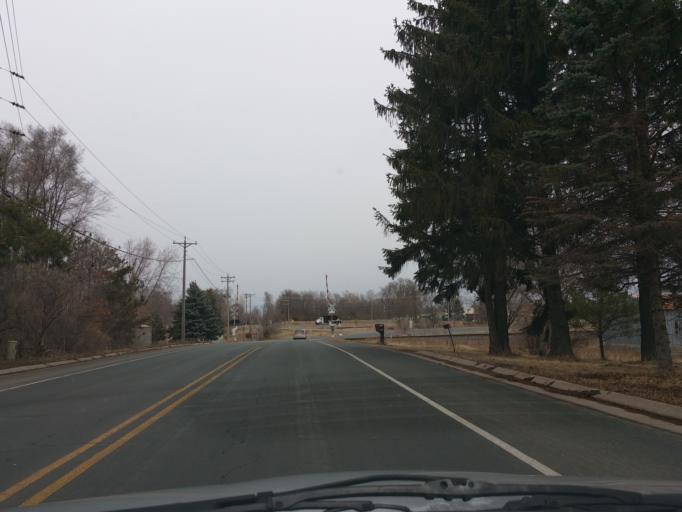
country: US
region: Wisconsin
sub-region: Saint Croix County
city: North Hudson
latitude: 44.9895
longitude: -92.7056
